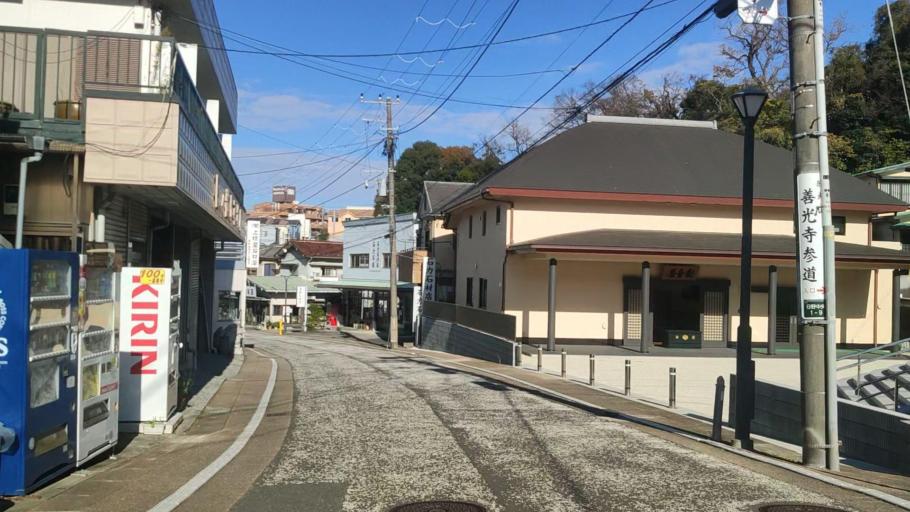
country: JP
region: Kanagawa
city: Yokohama
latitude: 35.3915
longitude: 139.5867
